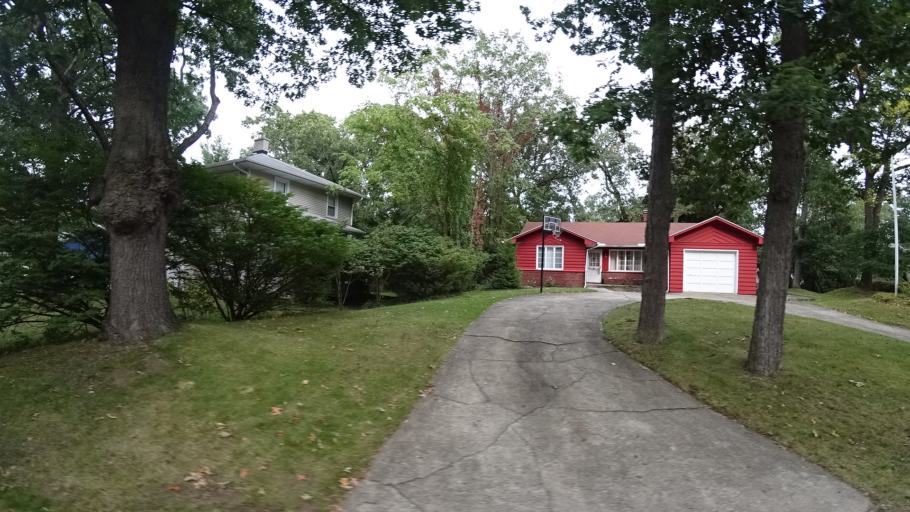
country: US
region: Indiana
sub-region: LaPorte County
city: Long Beach
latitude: 41.7433
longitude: -86.8563
